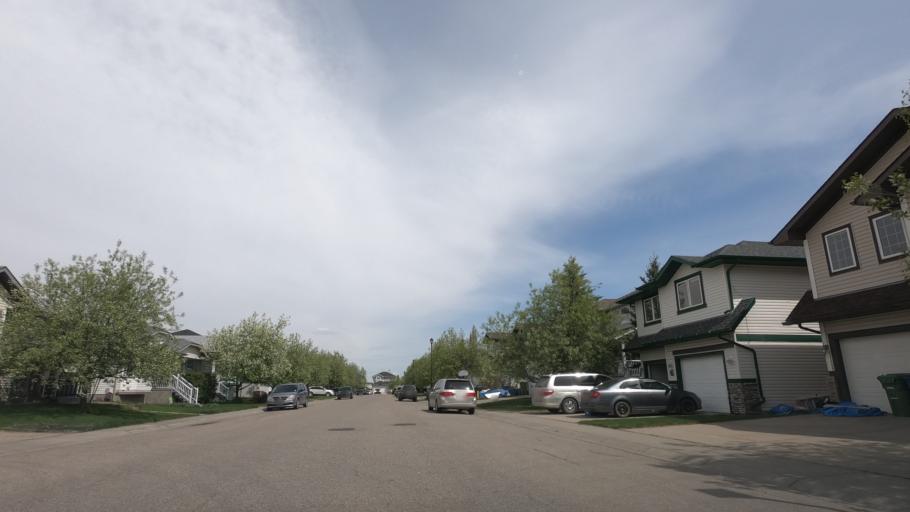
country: CA
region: Alberta
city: Airdrie
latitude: 51.3021
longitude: -114.0233
